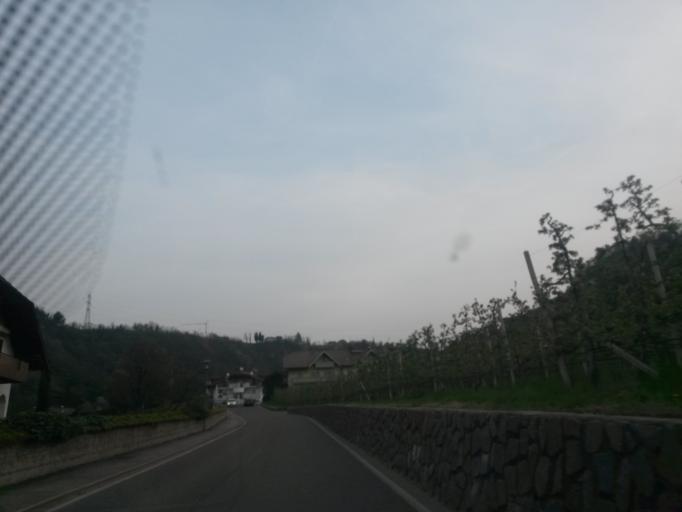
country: IT
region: Trentino-Alto Adige
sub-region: Bolzano
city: San Paolo
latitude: 46.4843
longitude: 11.2634
